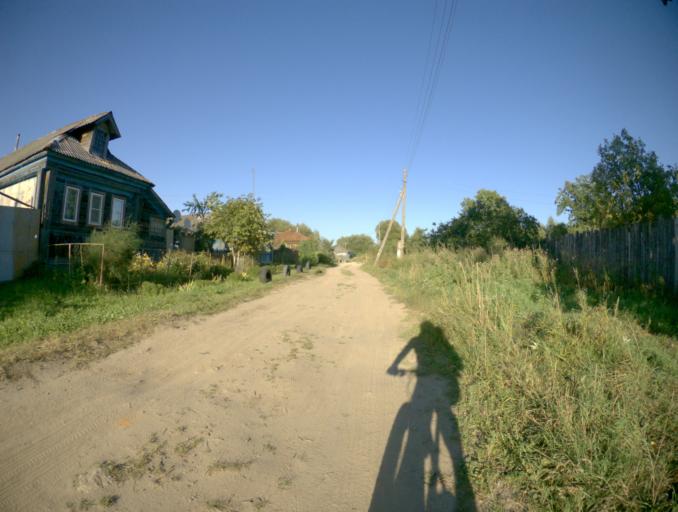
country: RU
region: Vladimir
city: Lakinsk
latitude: 55.8811
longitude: 39.8429
